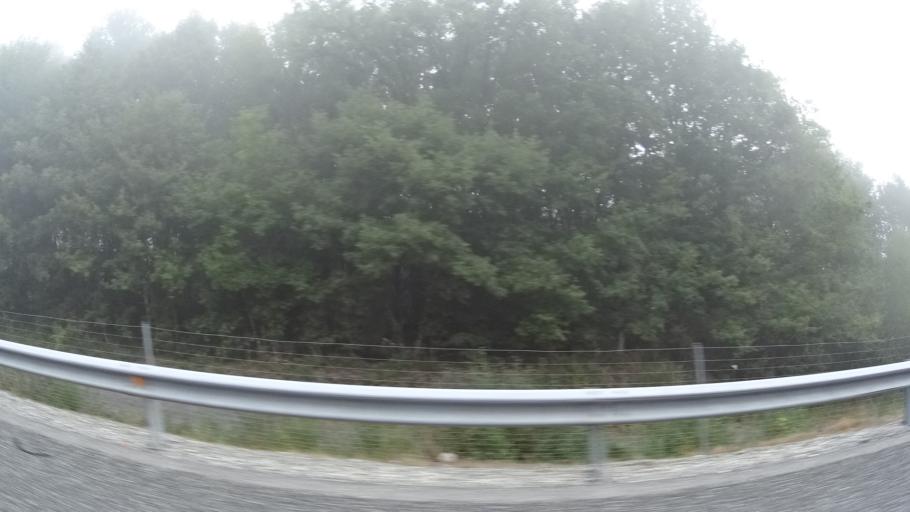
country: ES
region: Galicia
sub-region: Provincia de Lugo
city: Corgo
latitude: 42.9365
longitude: -7.3853
